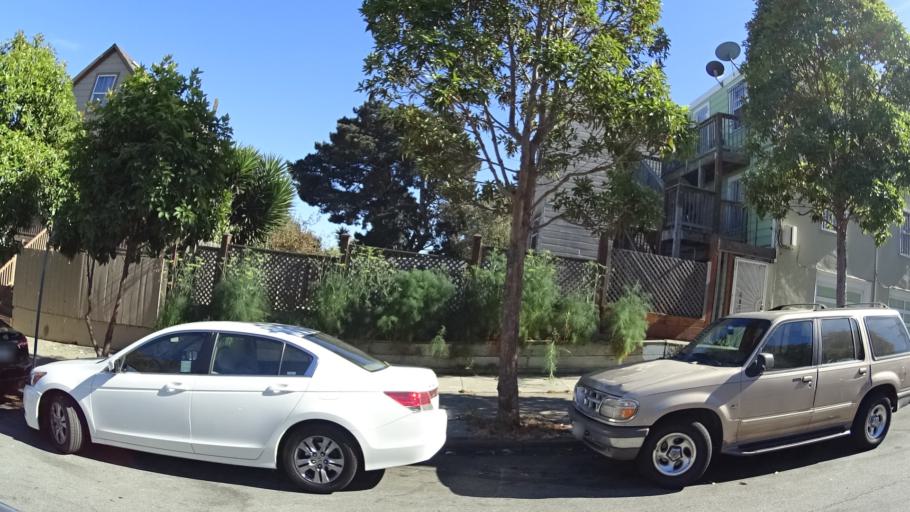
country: US
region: California
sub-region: San Mateo County
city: Brisbane
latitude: 37.7201
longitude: -122.3922
